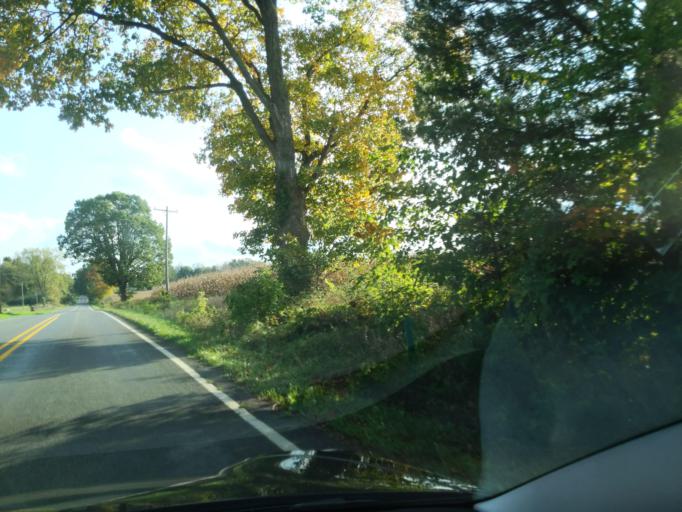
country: US
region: Michigan
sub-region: Ingham County
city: Leslie
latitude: 42.3671
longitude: -84.4629
